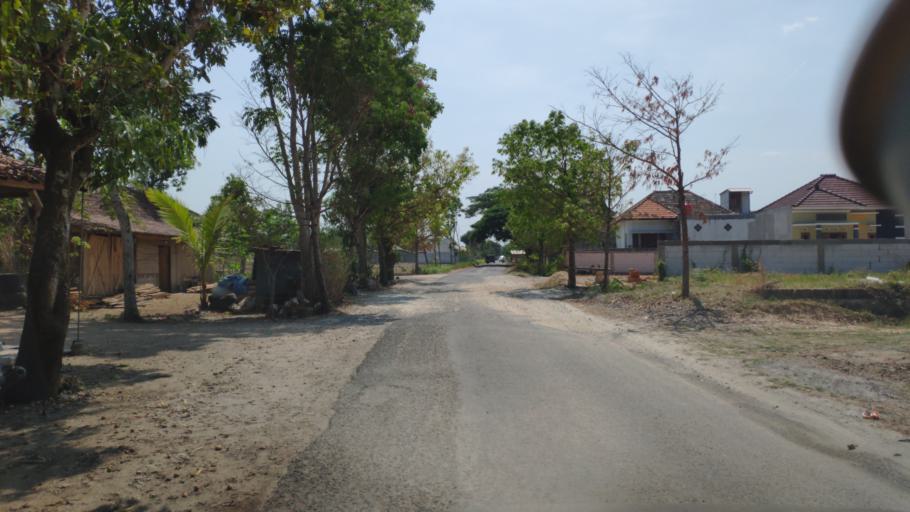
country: ID
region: Central Java
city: Bangkle
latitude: -6.9813
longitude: 111.4339
